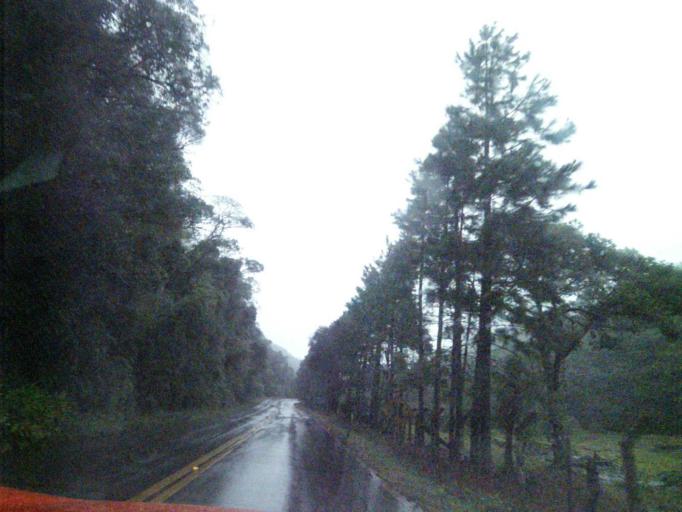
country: BR
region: Santa Catarina
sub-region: Anitapolis
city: Anitapolis
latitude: -27.7683
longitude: -49.0396
